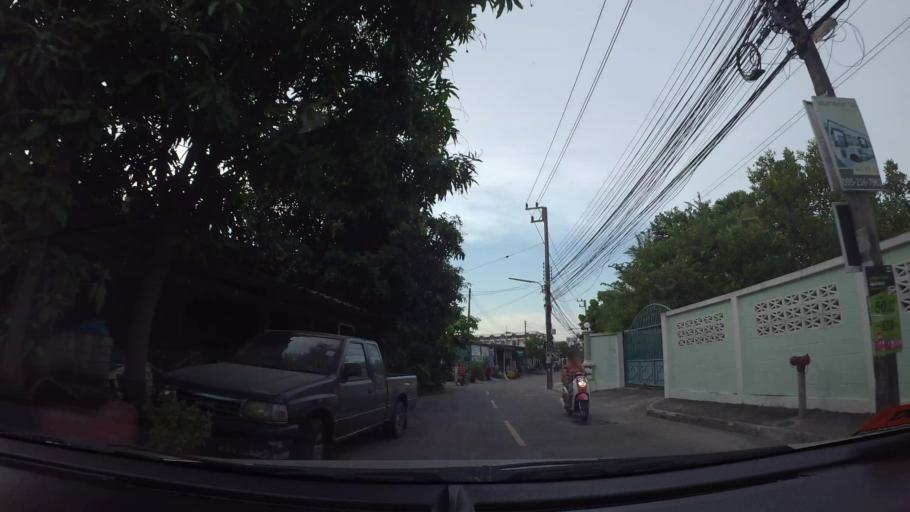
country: TH
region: Chon Buri
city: Chon Buri
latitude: 13.3425
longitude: 100.9819
